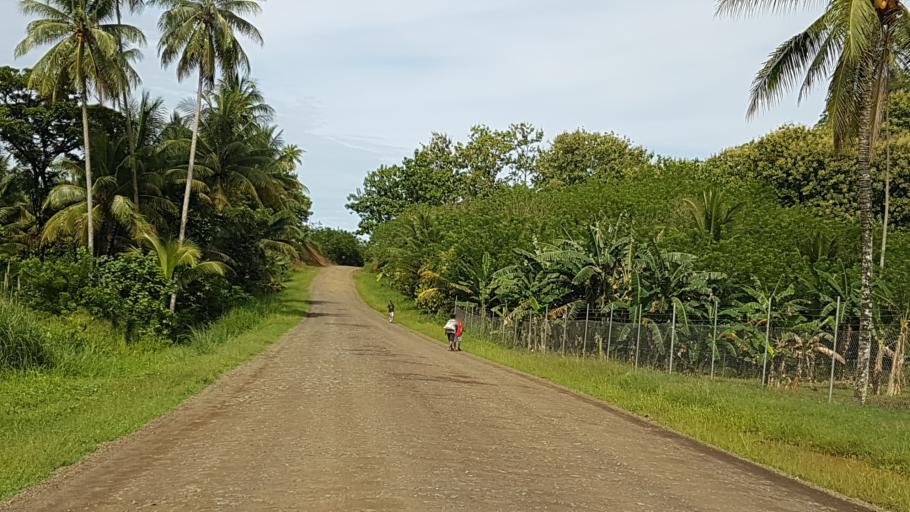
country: PG
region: Milne Bay
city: Alotau
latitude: -10.3397
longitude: 150.6406
